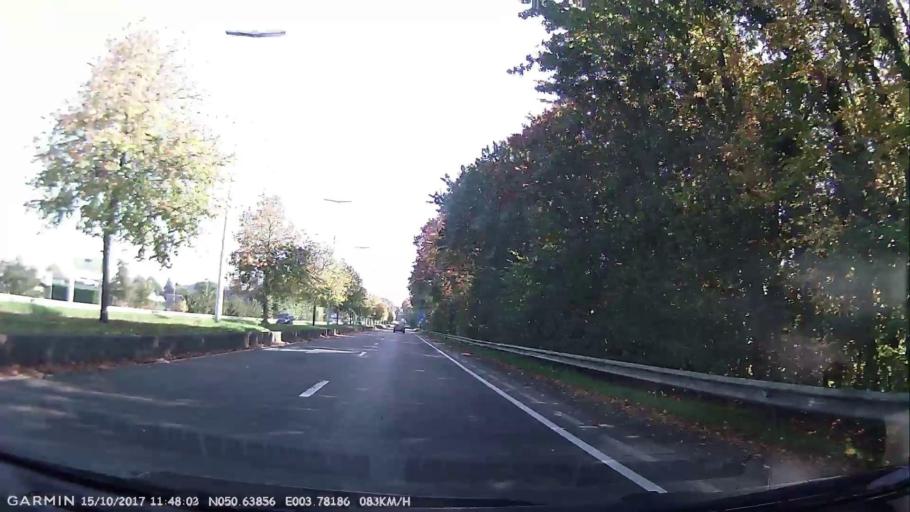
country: BE
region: Wallonia
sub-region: Province du Hainaut
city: Ath
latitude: 50.6386
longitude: 3.7819
